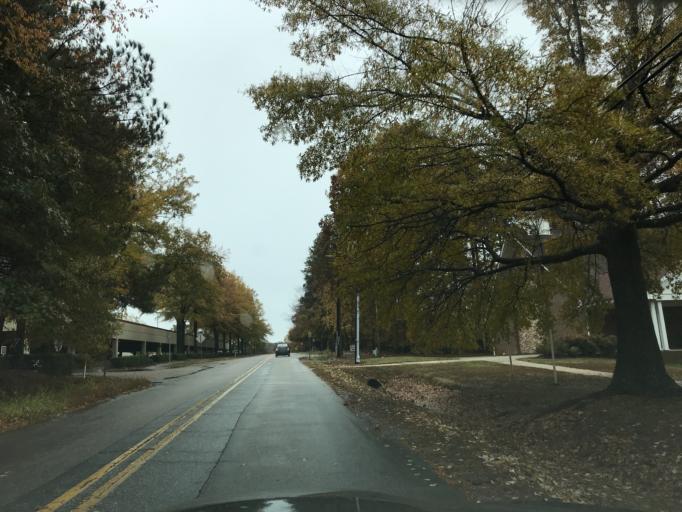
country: US
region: North Carolina
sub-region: Wake County
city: West Raleigh
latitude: 35.8433
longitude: -78.6146
